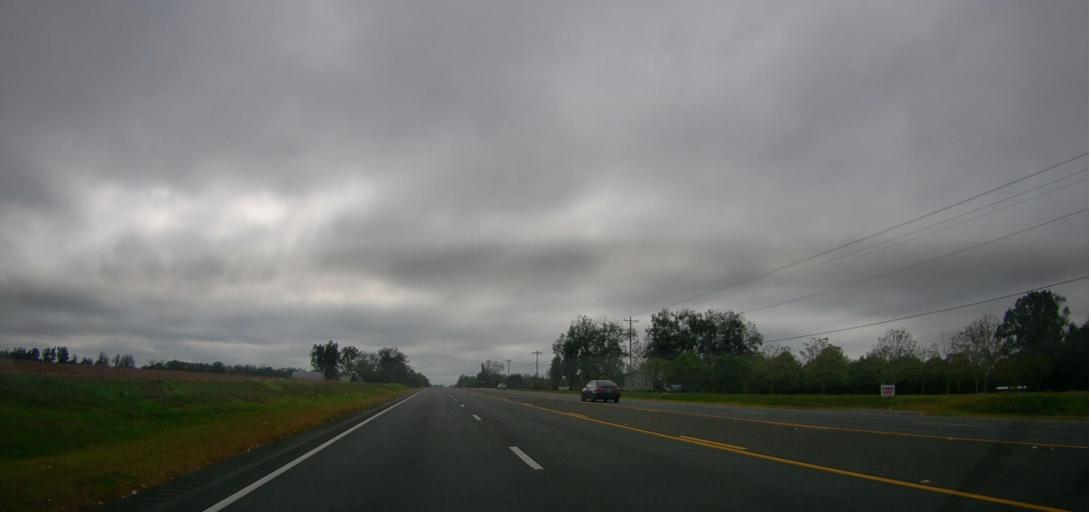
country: US
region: Georgia
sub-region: Thomas County
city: Thomasville
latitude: 30.9666
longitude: -83.8924
